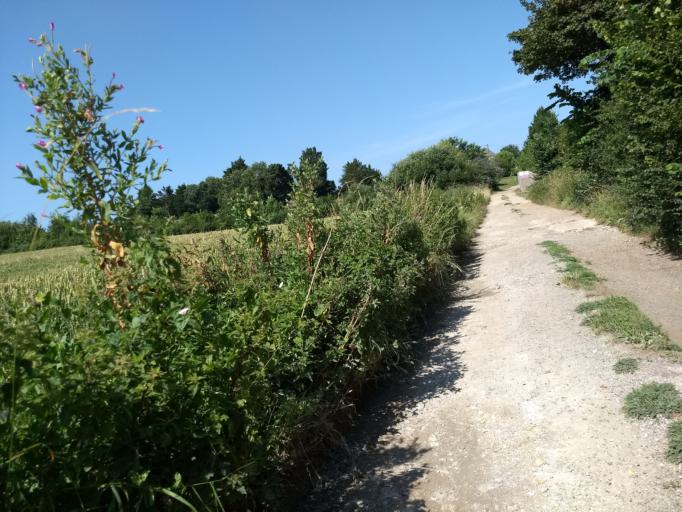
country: GB
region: England
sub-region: Isle of Wight
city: Newport
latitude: 50.6947
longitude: -1.3253
